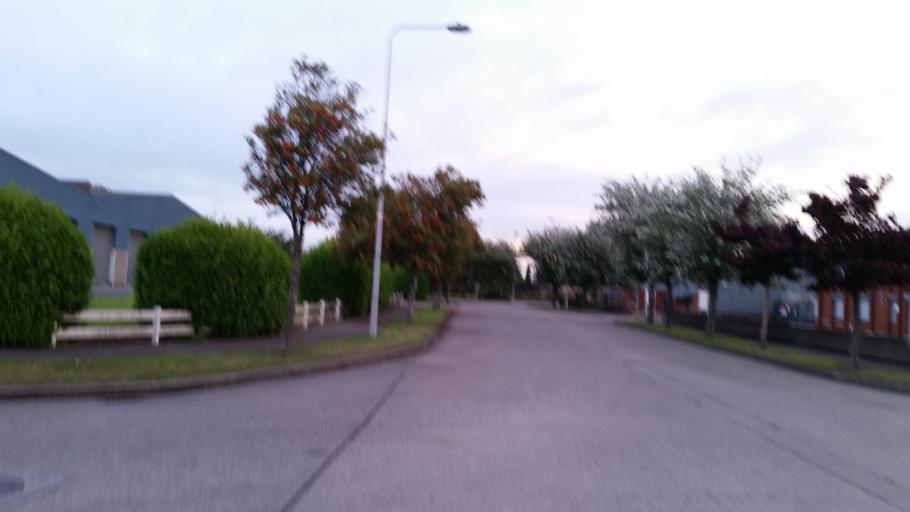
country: IE
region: Leinster
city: Beaumont
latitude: 53.4062
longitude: -6.2354
